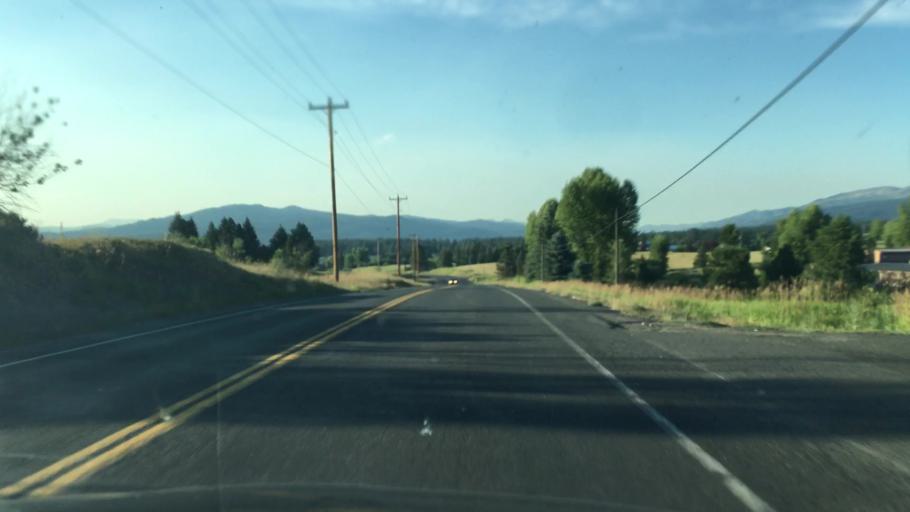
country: US
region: Idaho
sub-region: Valley County
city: McCall
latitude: 44.8806
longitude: -116.0907
